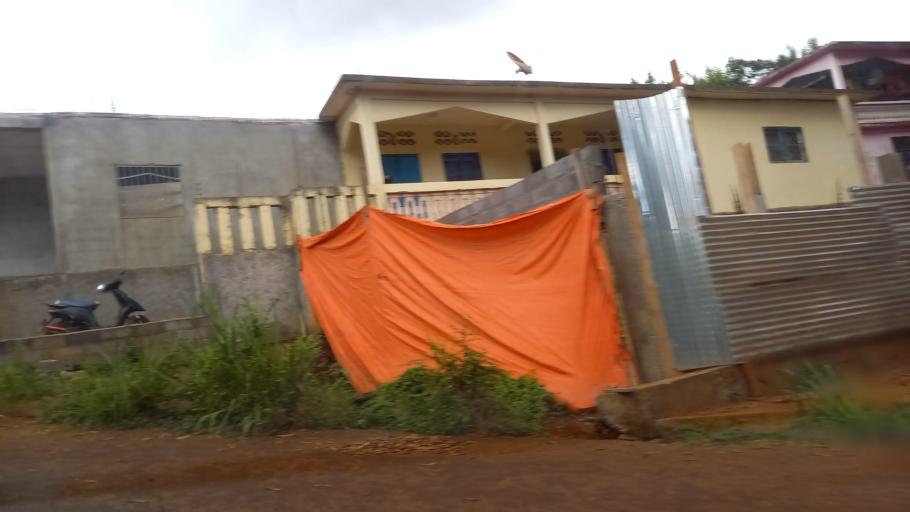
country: YT
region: Ouangani
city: Ouangani
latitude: -12.8348
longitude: 45.1314
